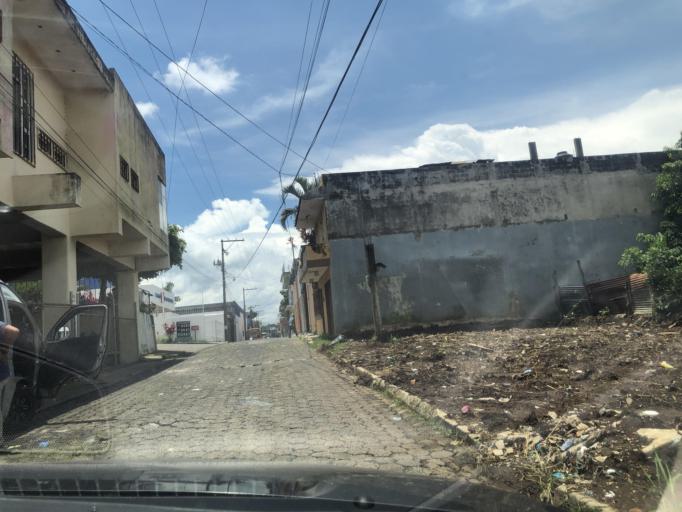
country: GT
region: Quetzaltenango
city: Coatepeque
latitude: 14.7077
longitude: -91.8675
